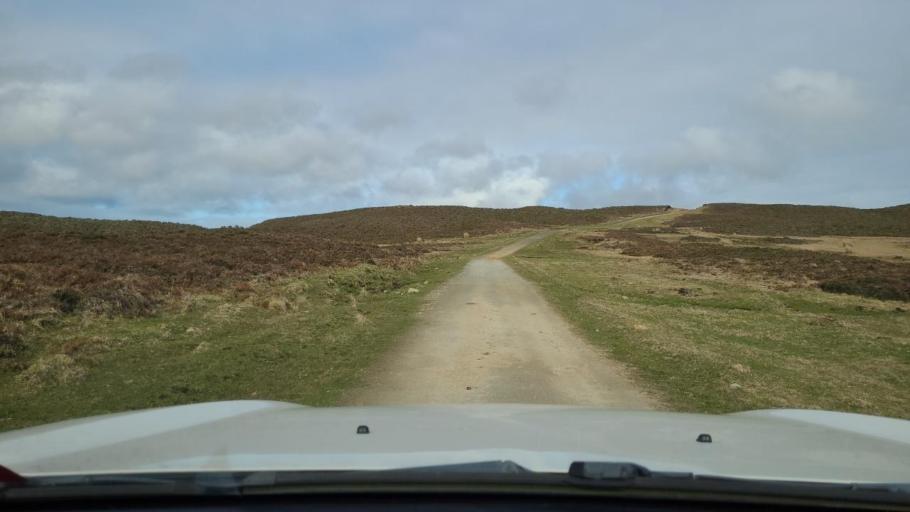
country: NZ
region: Chatham Islands
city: Waitangi
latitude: -44.0497
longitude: -176.6350
